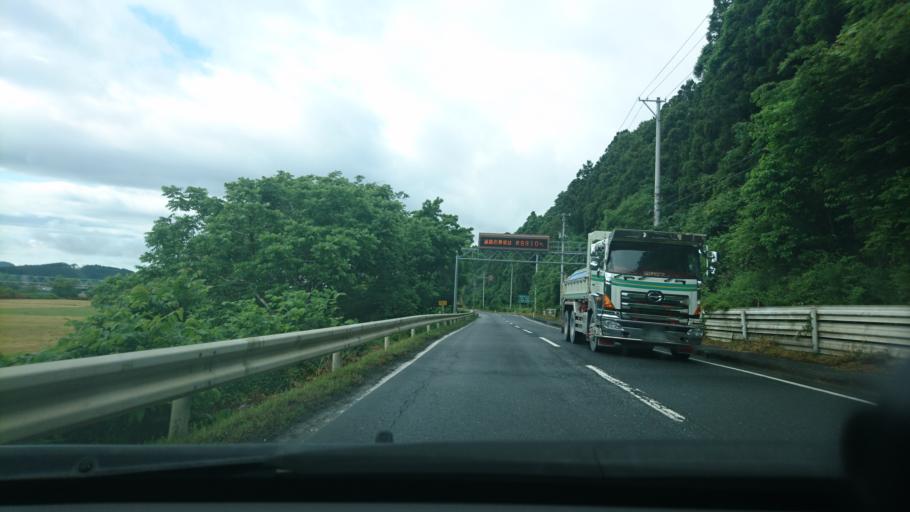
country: JP
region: Miyagi
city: Wakuya
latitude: 38.5972
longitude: 141.3039
